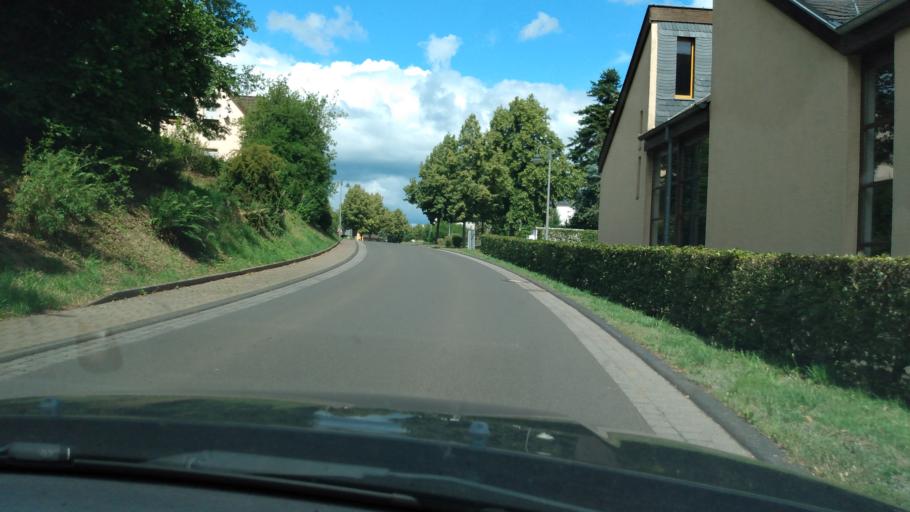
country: DE
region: Rheinland-Pfalz
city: Minderlittgen
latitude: 50.0092
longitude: 6.8364
